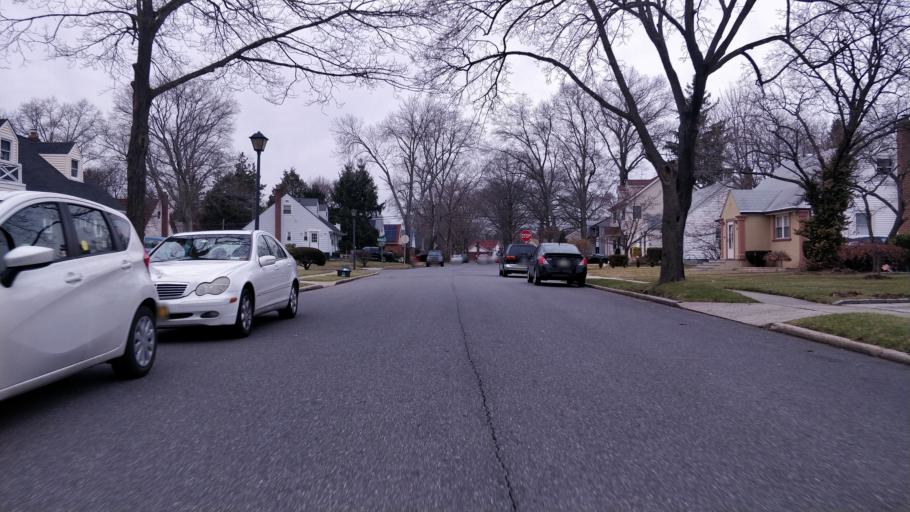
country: US
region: New York
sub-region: Nassau County
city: New Cassel
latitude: 40.7728
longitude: -73.5642
